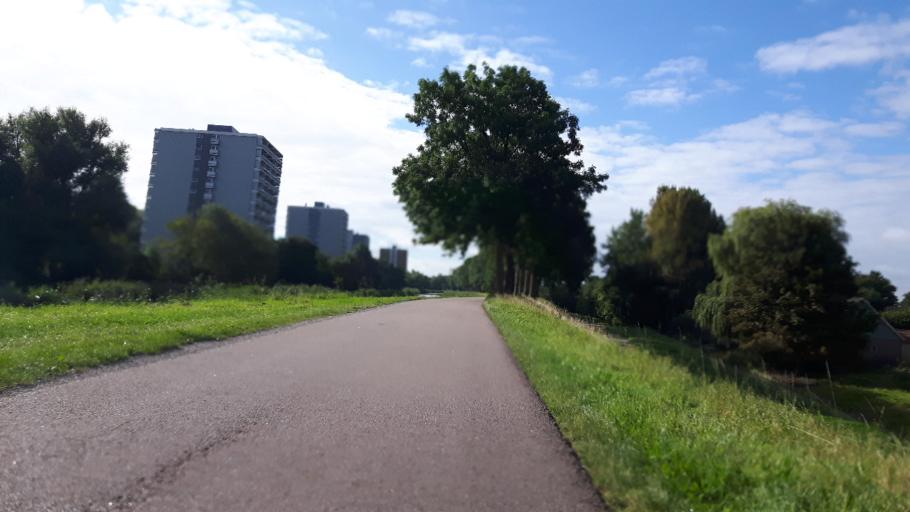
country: NL
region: North Holland
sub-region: Gemeente Purmerend
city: Purmerend
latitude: 52.5272
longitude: 4.9561
